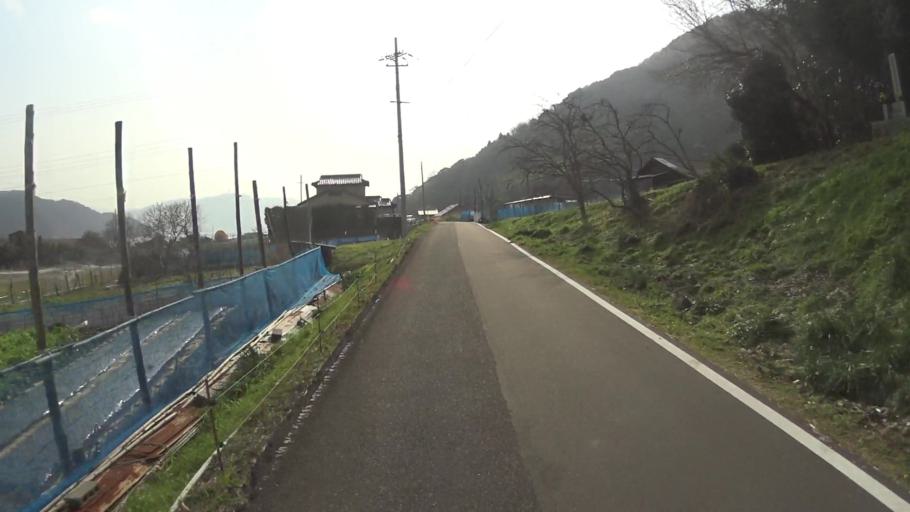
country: JP
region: Kyoto
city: Maizuru
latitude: 35.5061
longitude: 135.3334
